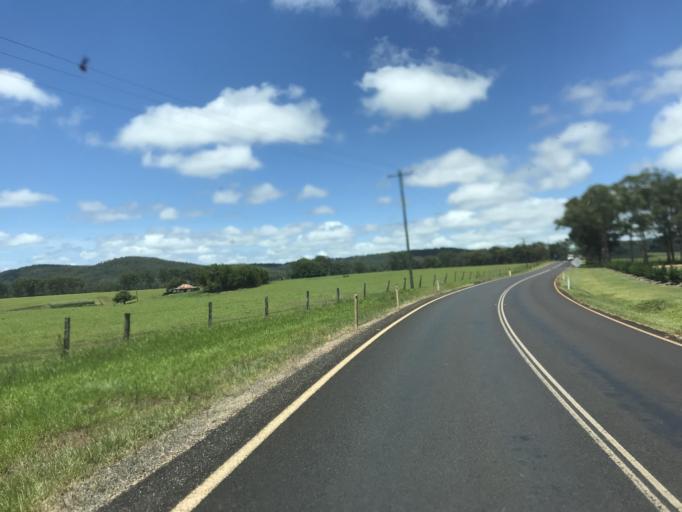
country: AU
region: Queensland
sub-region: Tablelands
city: Ravenshoe
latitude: -17.5135
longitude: 145.4506
